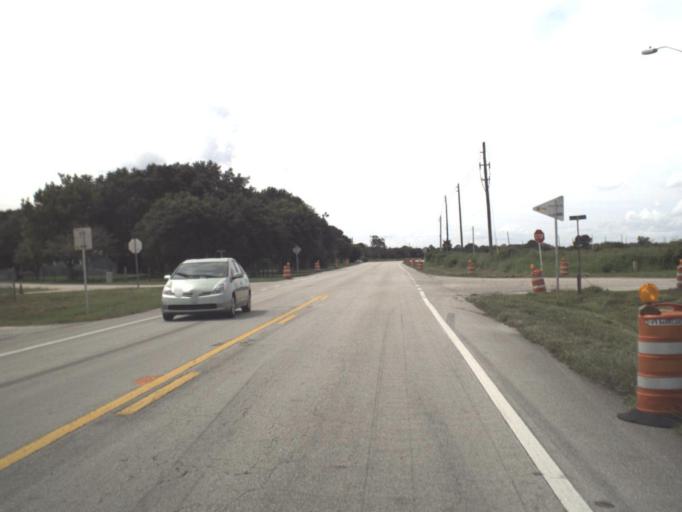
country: US
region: Florida
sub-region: Okeechobee County
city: Taylor Creek
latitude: 27.2619
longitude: -80.7433
